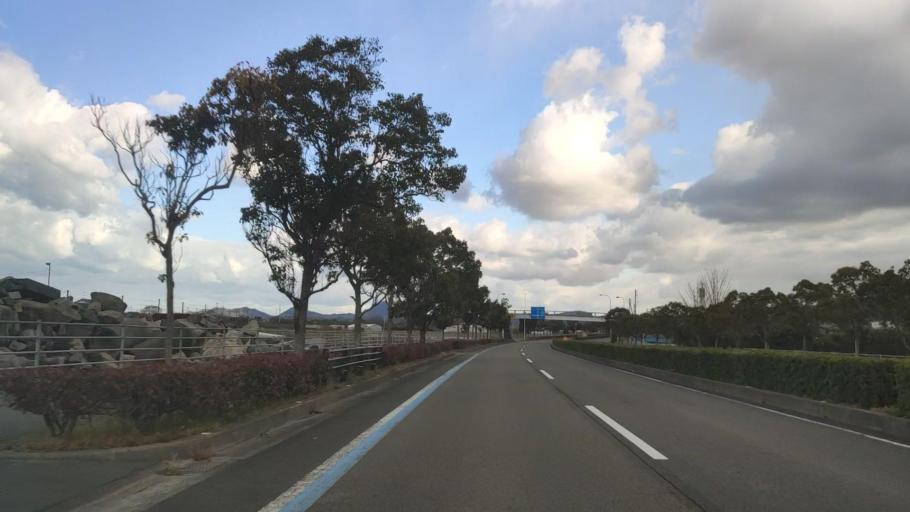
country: JP
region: Ehime
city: Hojo
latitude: 33.9320
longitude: 132.7661
